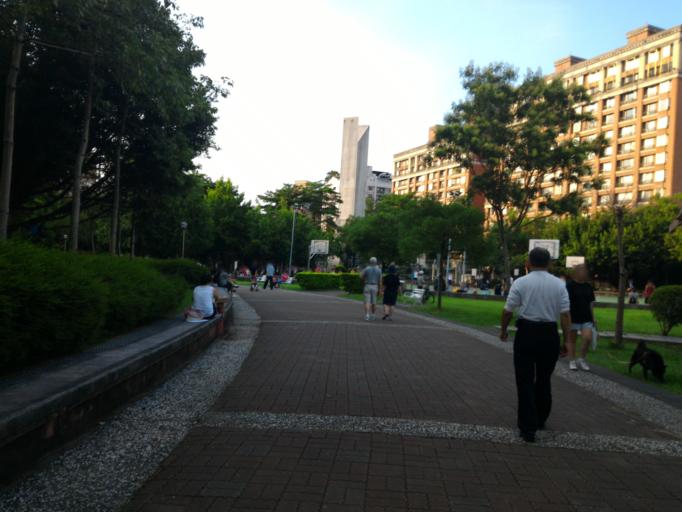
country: TW
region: Taipei
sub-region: Taipei
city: Banqiao
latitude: 25.0021
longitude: 121.5142
